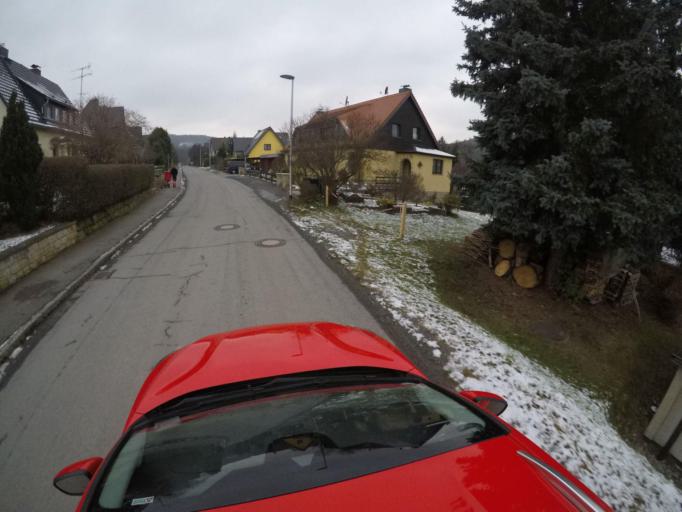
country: DE
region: Saxony
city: Dohma
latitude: 50.8761
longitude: 13.9544
